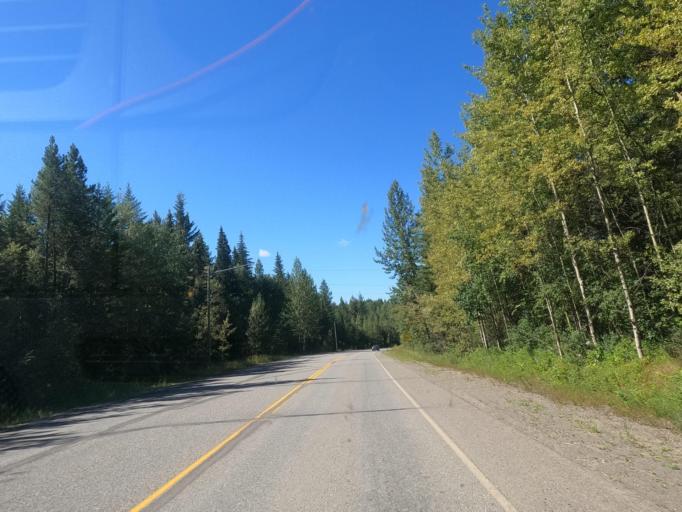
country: CA
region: British Columbia
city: Quesnel
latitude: 53.0181
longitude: -122.4777
